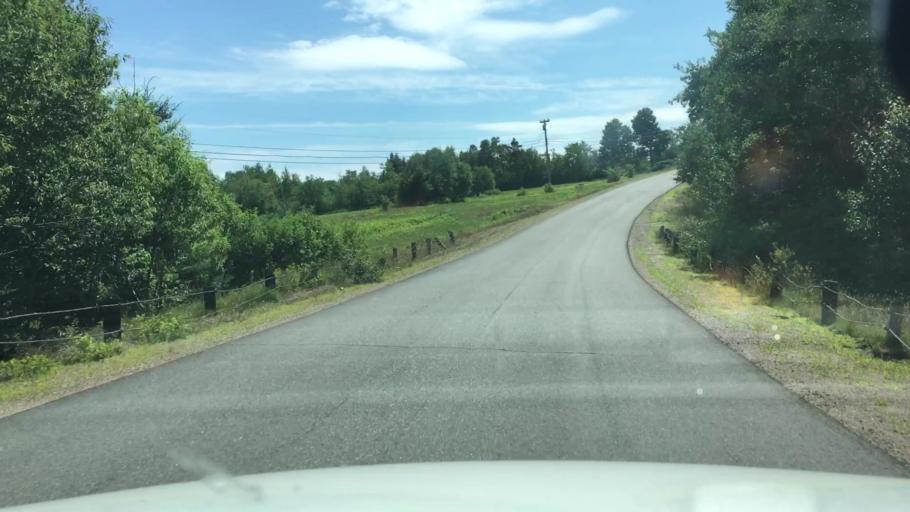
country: CA
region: New Brunswick
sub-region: Charlotte County
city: Saint Andrews
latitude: 44.9937
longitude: -67.0656
